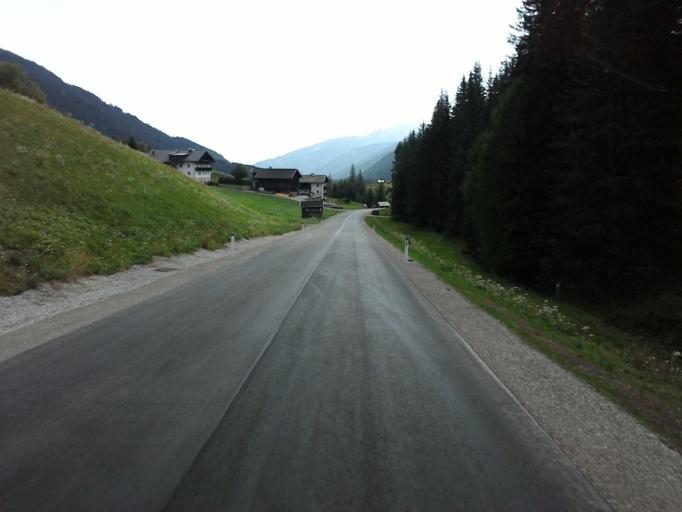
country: AT
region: Tyrol
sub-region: Politischer Bezirk Lienz
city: Abfaltersbach
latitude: 46.7153
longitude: 12.5588
